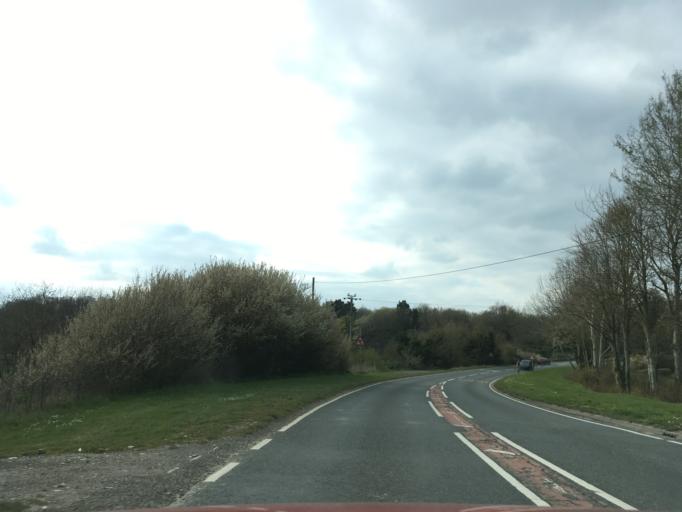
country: GB
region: England
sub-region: Oxfordshire
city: Kidlington
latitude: 51.8611
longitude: -1.3060
